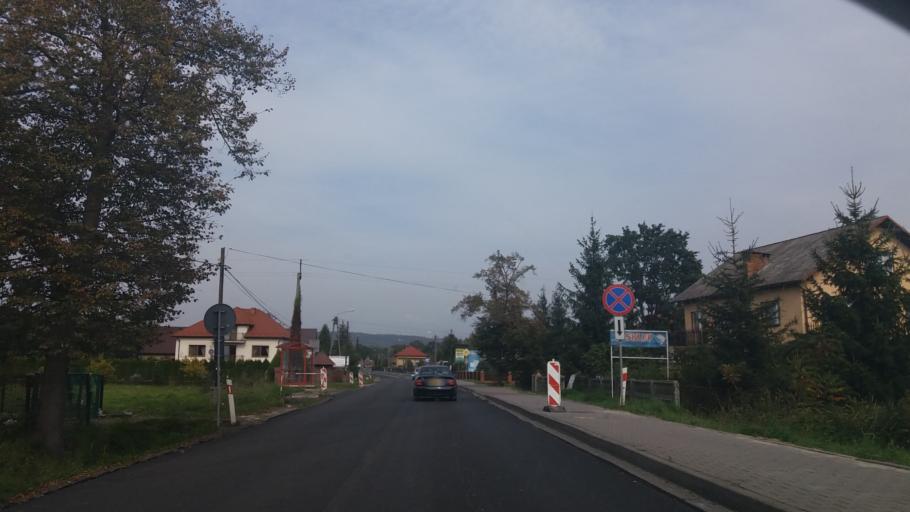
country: PL
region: Lesser Poland Voivodeship
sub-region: Powiat chrzanowski
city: Babice
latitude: 50.0476
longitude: 19.4479
